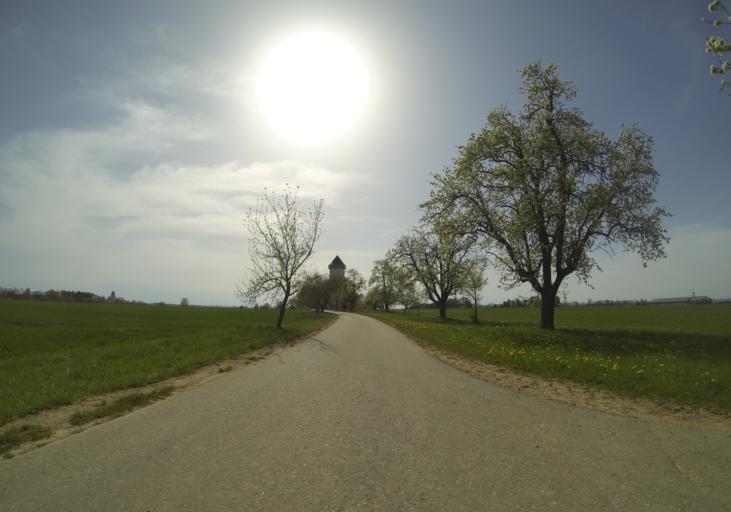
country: DE
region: Baden-Wuerttemberg
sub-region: Tuebingen Region
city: Huttisheim
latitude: 48.2840
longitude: 9.9543
